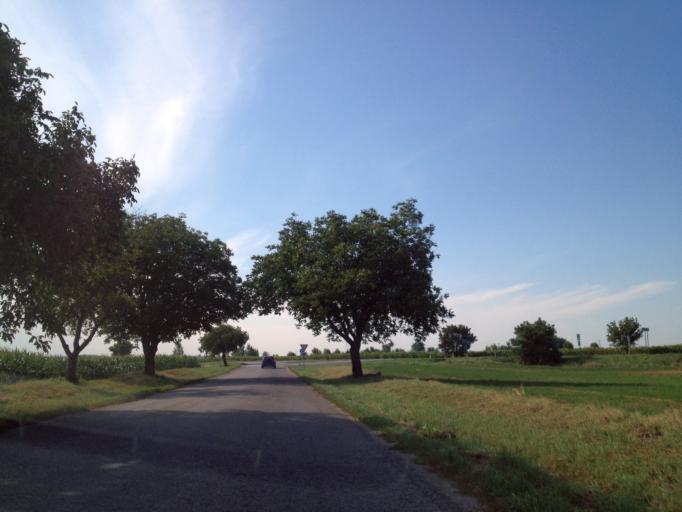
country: SK
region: Nitriansky
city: Svodin
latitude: 47.8865
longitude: 18.4174
